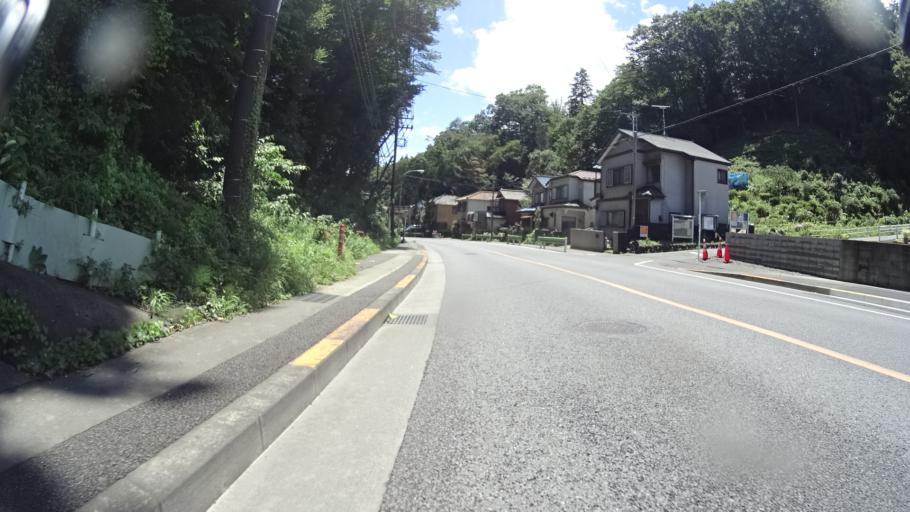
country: JP
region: Tokyo
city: Ome
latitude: 35.8025
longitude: 139.2653
